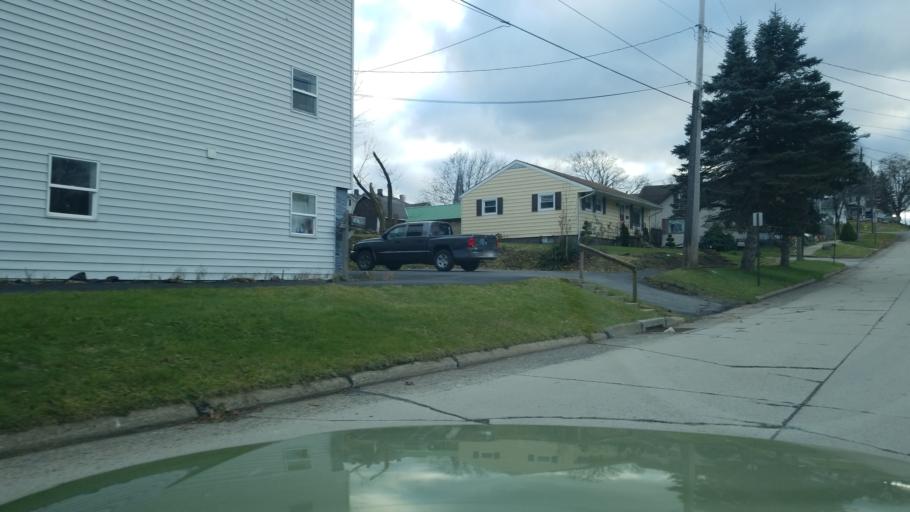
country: US
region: Pennsylvania
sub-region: Clearfield County
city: DuBois
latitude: 41.1227
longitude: -78.7703
